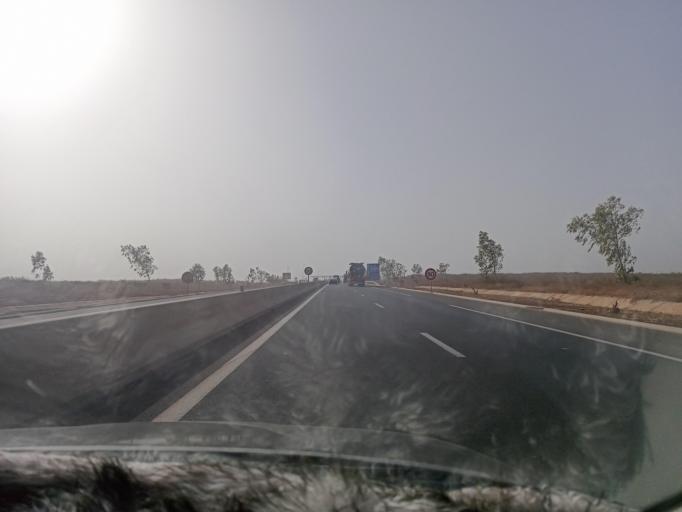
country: SN
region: Thies
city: Pout
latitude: 14.7097
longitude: -17.0913
